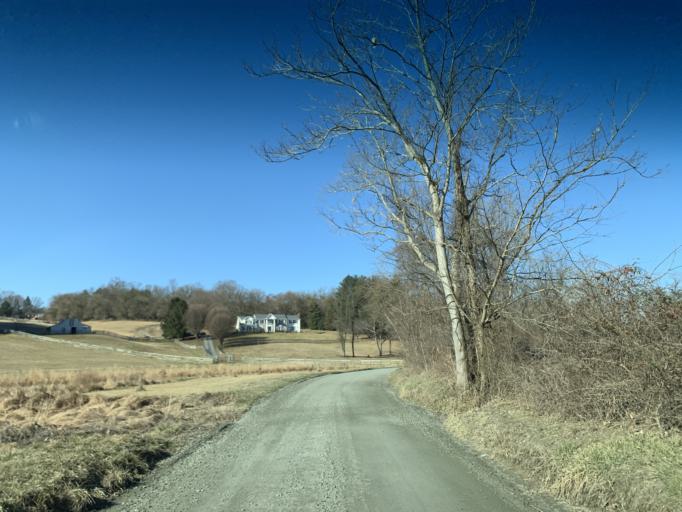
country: US
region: Maryland
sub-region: Harford County
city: Bel Air North
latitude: 39.6143
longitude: -76.3225
